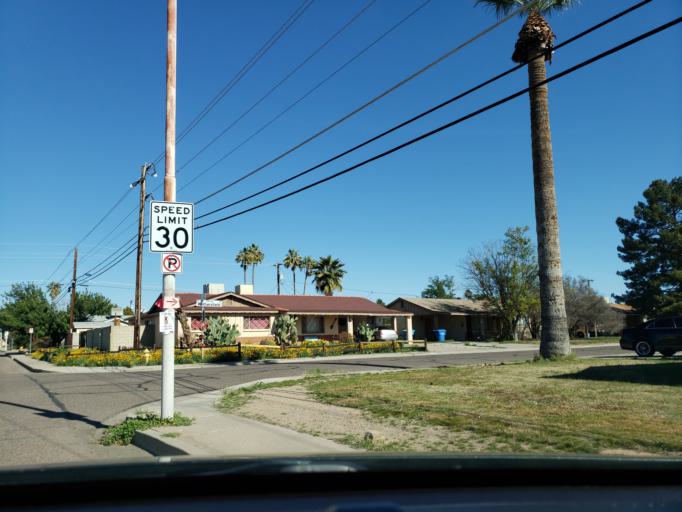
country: US
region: Arizona
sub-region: Maricopa County
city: Glendale
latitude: 33.5970
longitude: -112.1253
